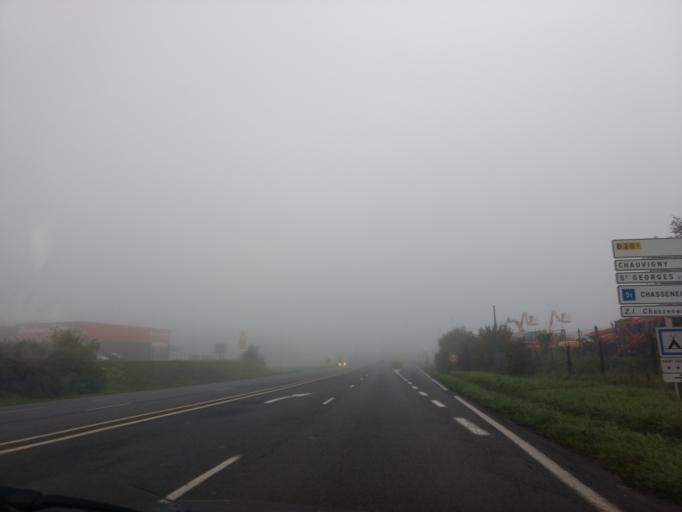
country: FR
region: Poitou-Charentes
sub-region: Departement de la Vienne
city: Chasseneuil-du-Poitou
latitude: 46.6657
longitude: 0.3722
